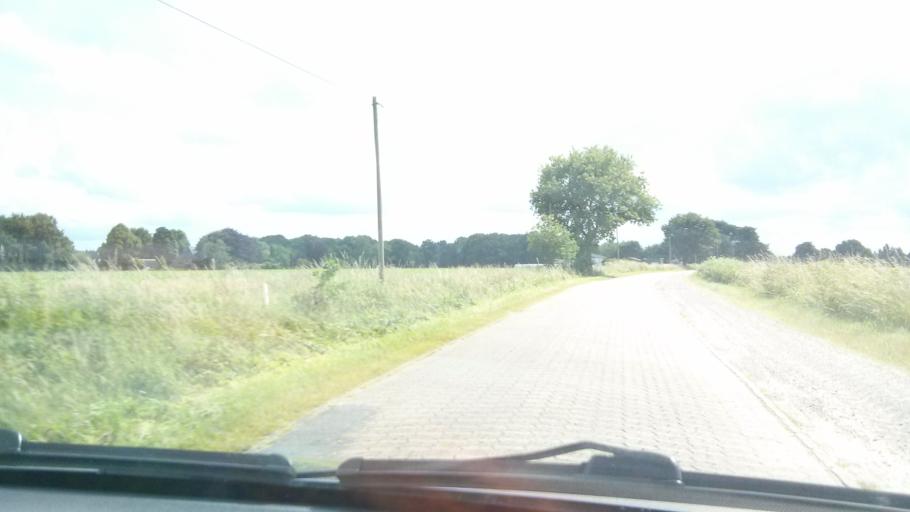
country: DE
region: Lower Saxony
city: Schiffdorf
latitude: 53.5065
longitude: 8.6959
